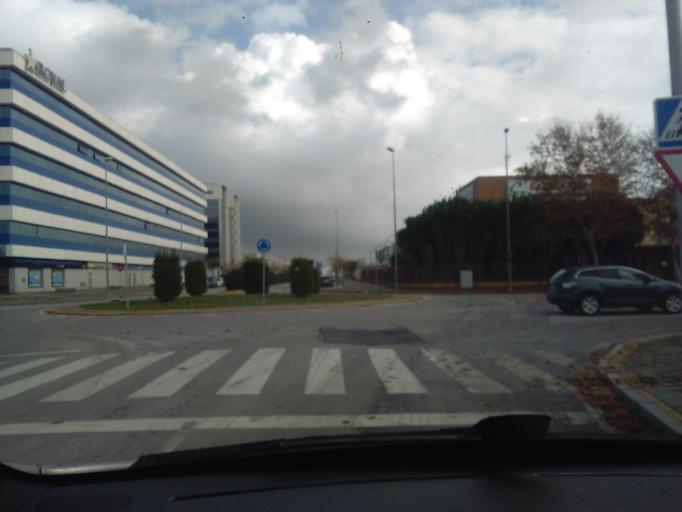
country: ES
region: Andalusia
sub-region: Provincia de Sevilla
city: Sevilla
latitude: 37.3817
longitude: -5.9195
